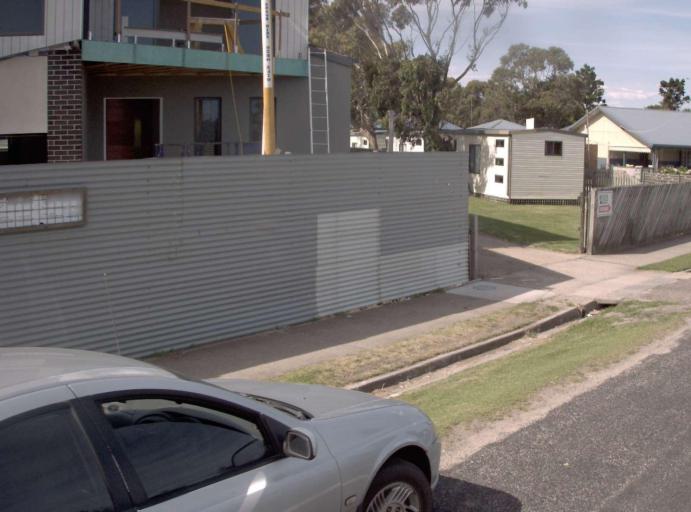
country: AU
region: Victoria
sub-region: East Gippsland
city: Lakes Entrance
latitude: -37.8785
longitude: 147.9966
